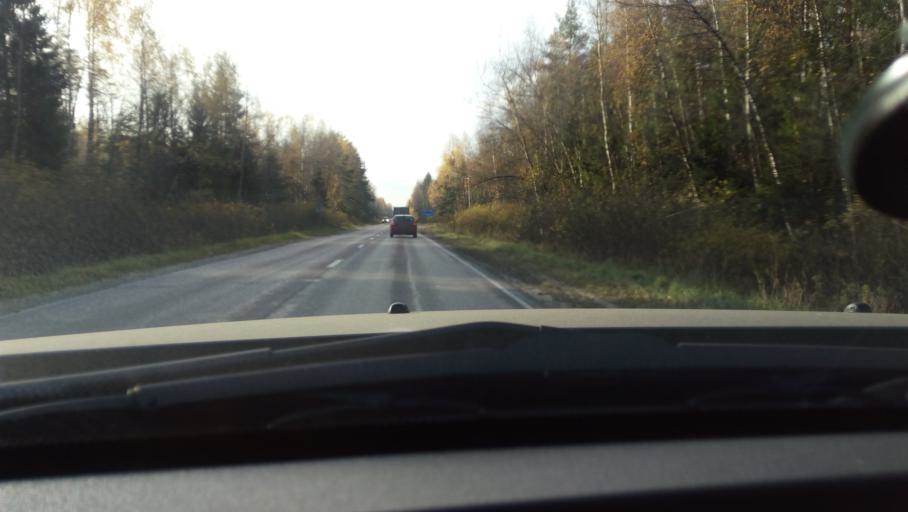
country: RU
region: Moskovskaya
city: Fryazevo
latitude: 55.7029
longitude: 38.4441
